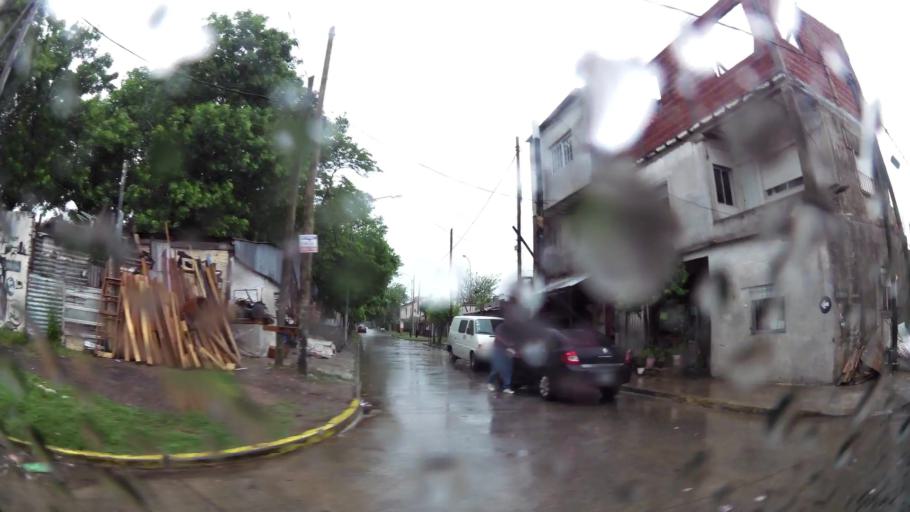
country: AR
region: Buenos Aires
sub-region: Partido de Lanus
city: Lanus
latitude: -34.7196
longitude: -58.4098
